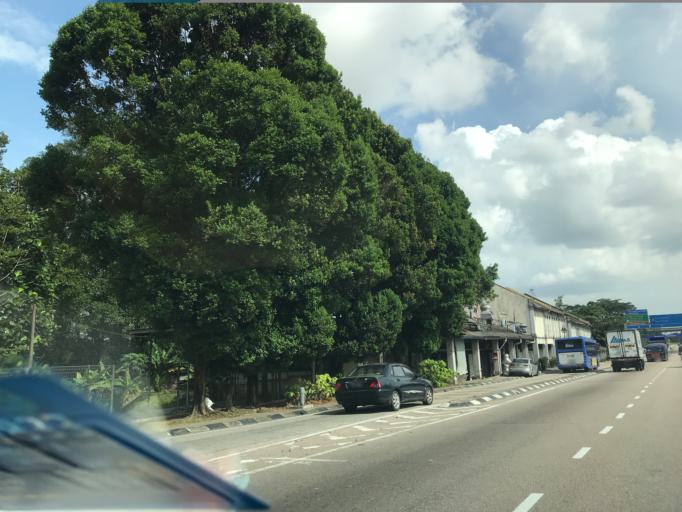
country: MY
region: Johor
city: Skudai
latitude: 1.5393
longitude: 103.6612
